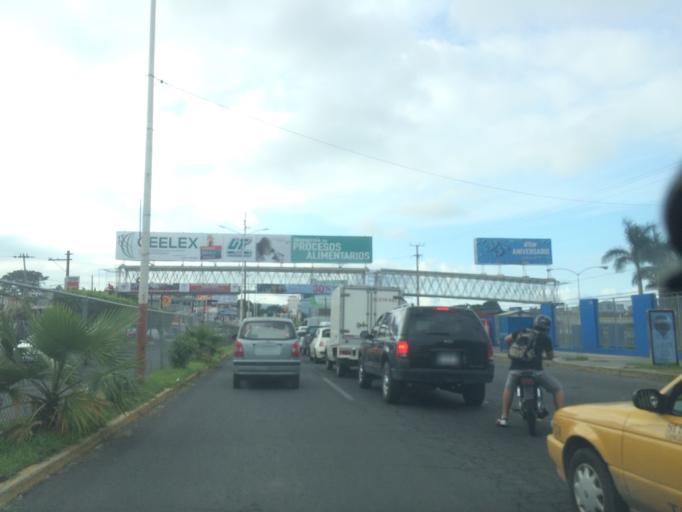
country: MX
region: Nayarit
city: Tepic
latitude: 21.4926
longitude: -104.8959
